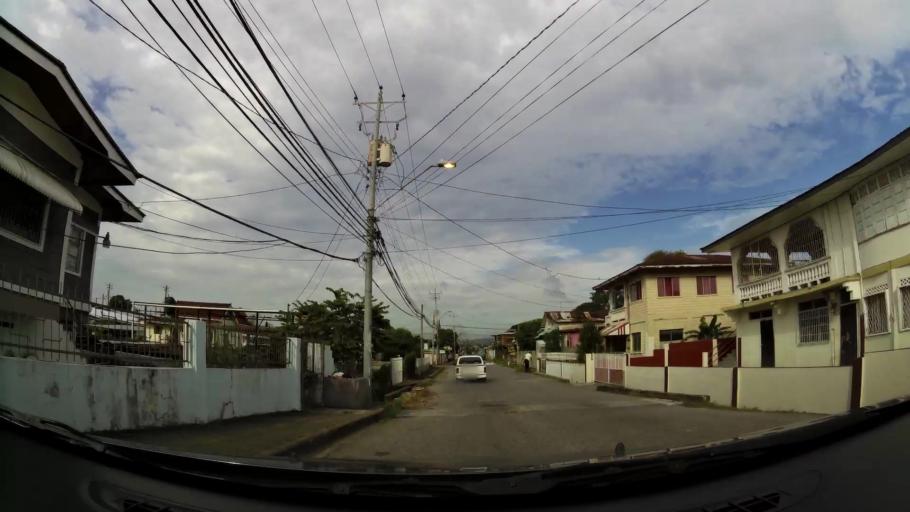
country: TT
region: San Juan/Laventille
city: Laventille
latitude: 10.6538
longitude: -61.4455
